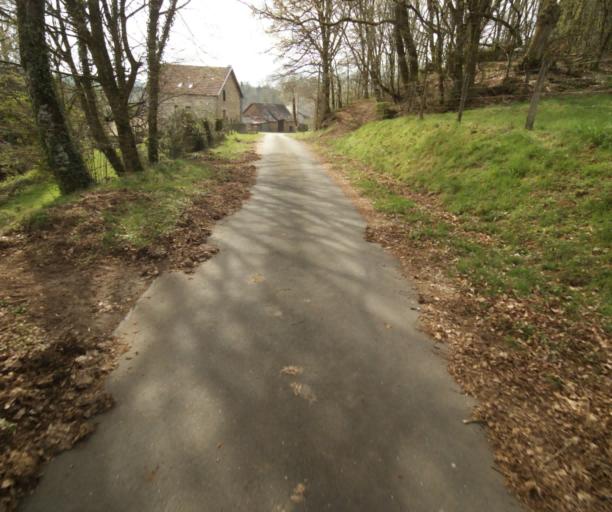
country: FR
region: Limousin
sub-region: Departement de la Correze
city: Correze
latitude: 45.3737
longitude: 1.8216
